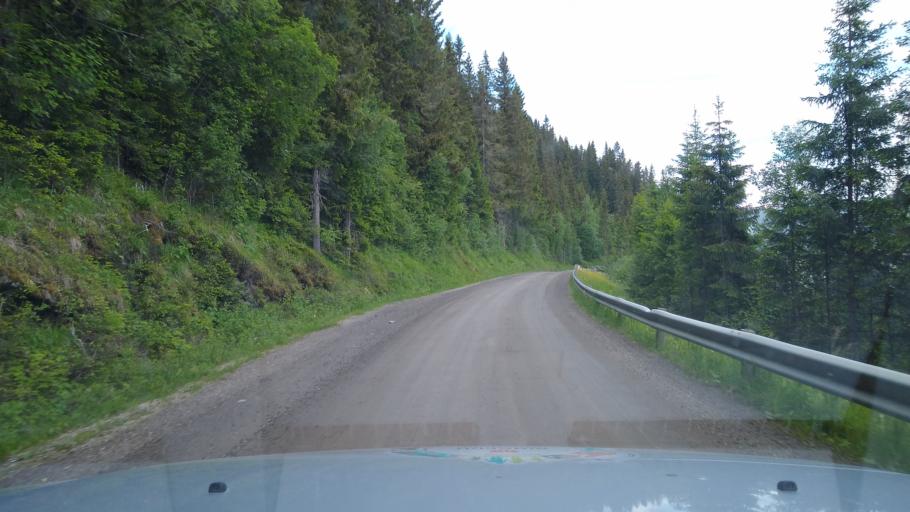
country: NO
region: Oppland
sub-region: Ringebu
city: Ringebu
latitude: 61.4985
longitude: 10.1425
